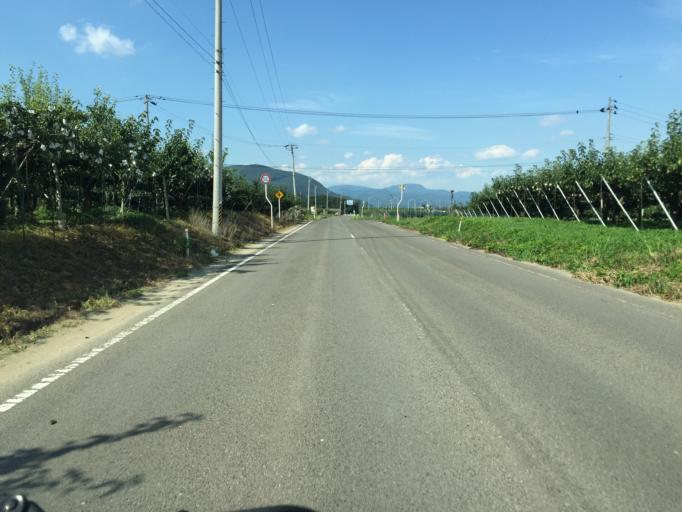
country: JP
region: Fukushima
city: Fukushima-shi
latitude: 37.7841
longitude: 140.3854
